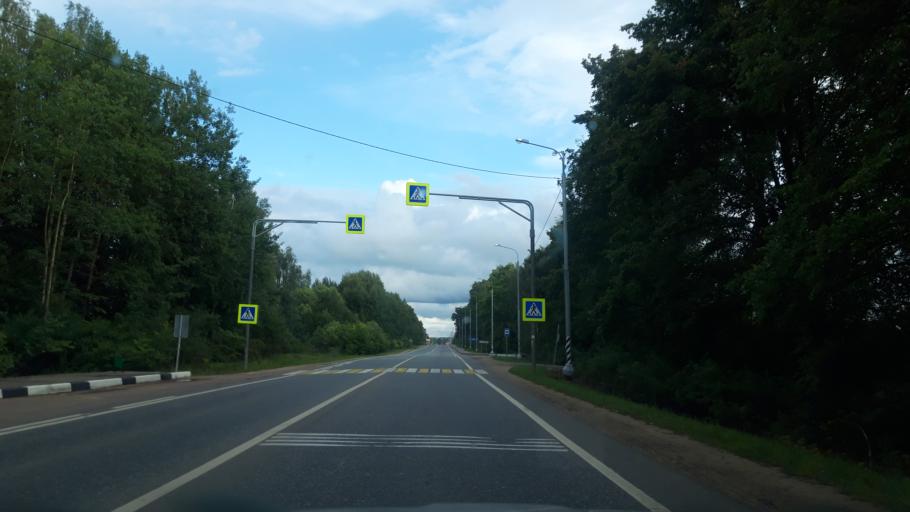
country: RU
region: Moskovskaya
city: Solnechnogorsk
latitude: 56.1294
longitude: 36.9262
